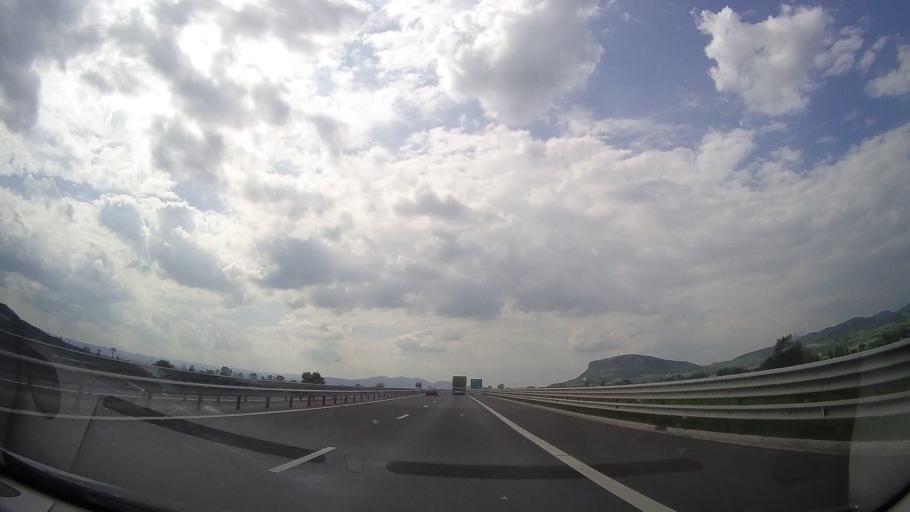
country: RO
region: Hunedoara
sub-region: Comuna Rapoltu Mare
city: Rapoltu Mare
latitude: 45.8432
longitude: 23.0757
